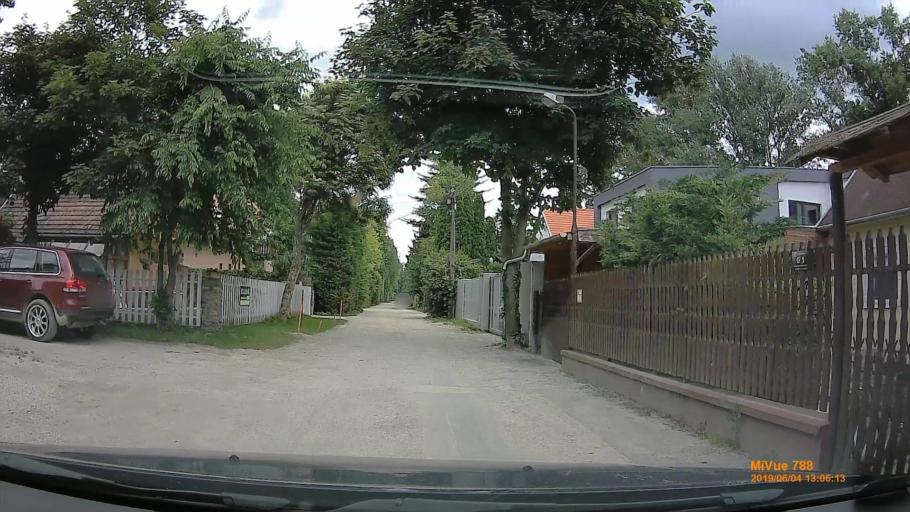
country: HU
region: Budapest
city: Budapest XXII. keruelet
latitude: 47.4016
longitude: 19.0206
